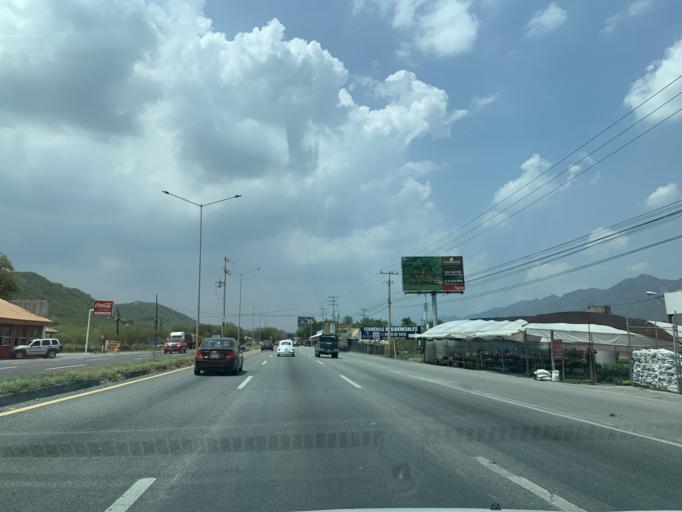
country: MX
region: Nuevo Leon
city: Santiago
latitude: 25.4563
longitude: -100.1665
